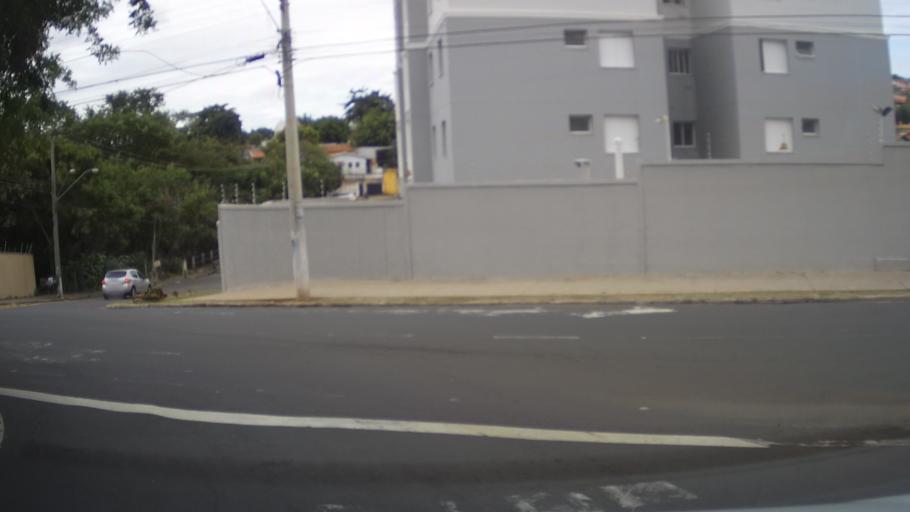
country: BR
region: Sao Paulo
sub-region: Campinas
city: Campinas
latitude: -22.8822
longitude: -47.0299
